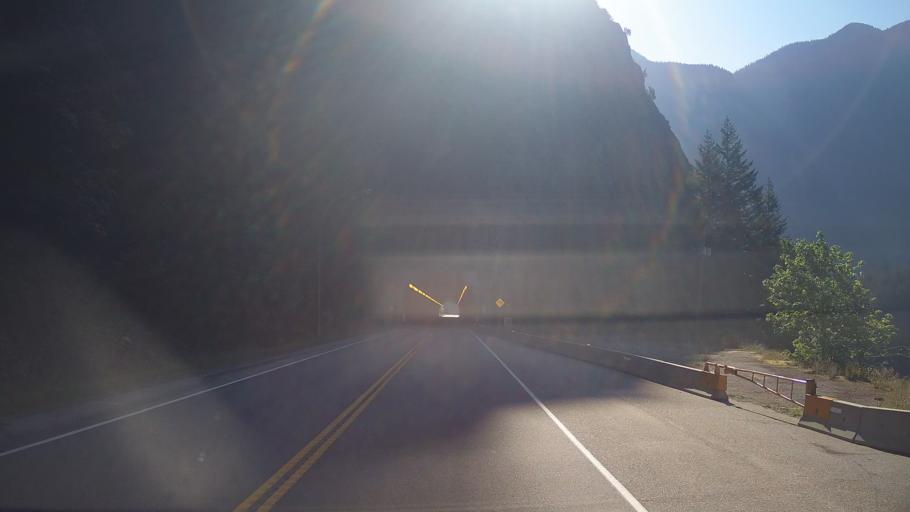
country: CA
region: British Columbia
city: Hope
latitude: 49.5630
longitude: -121.4156
